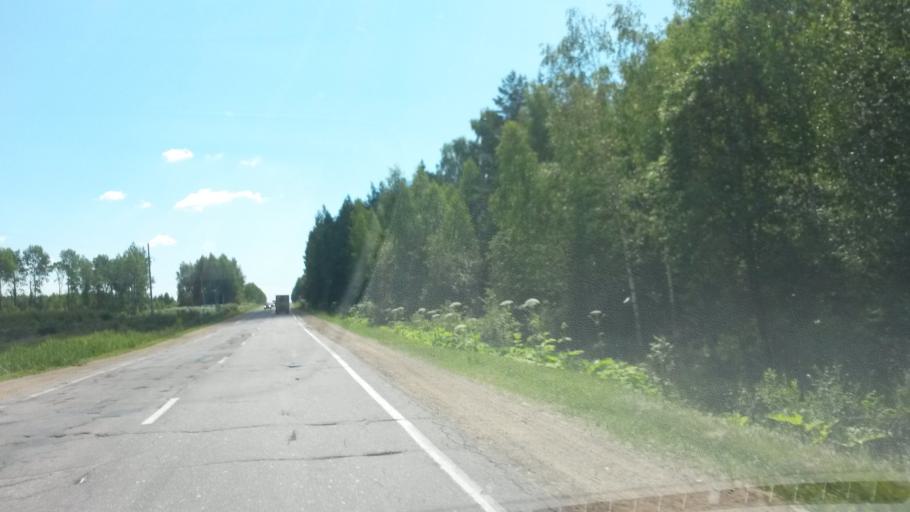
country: RU
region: Jaroslavl
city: Dubki
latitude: 57.2515
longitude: 40.1158
